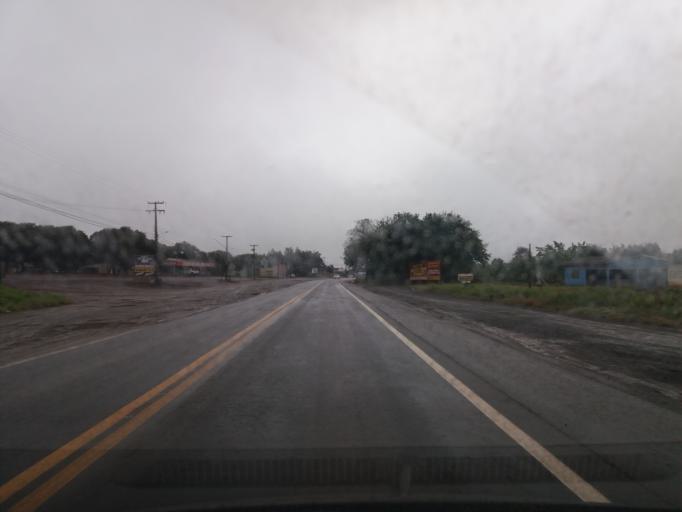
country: BR
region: Parana
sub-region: Realeza
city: Realeza
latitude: -25.5011
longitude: -53.5975
